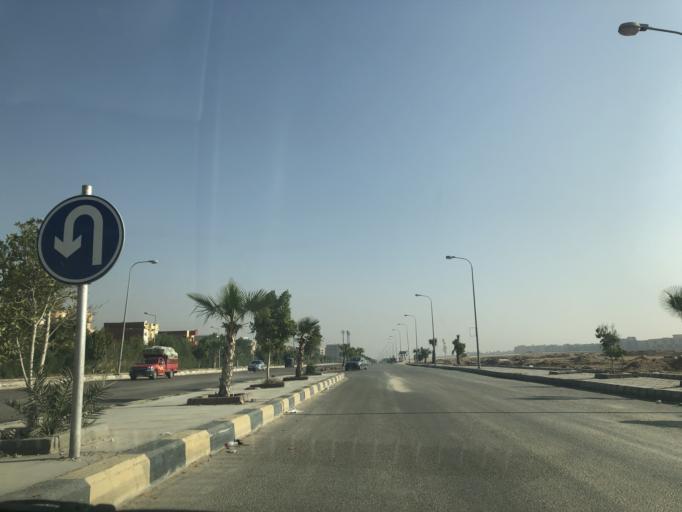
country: EG
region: Al Jizah
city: Madinat Sittah Uktubar
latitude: 29.9222
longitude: 31.0572
